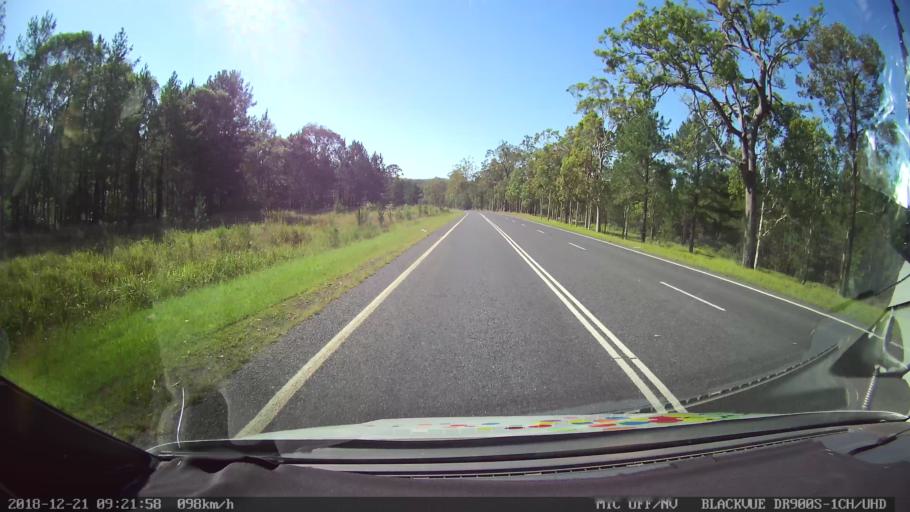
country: AU
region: New South Wales
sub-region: Clarence Valley
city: Maclean
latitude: -29.3362
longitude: 153.0014
